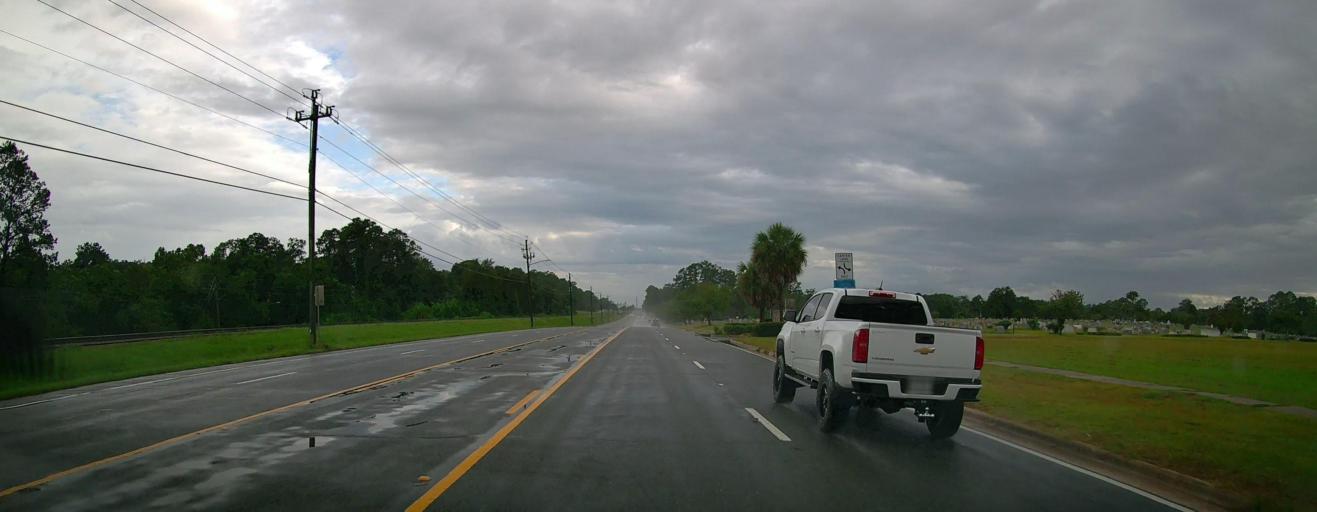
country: US
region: Georgia
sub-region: Ware County
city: Sunnyside
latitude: 31.2289
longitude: -82.3346
